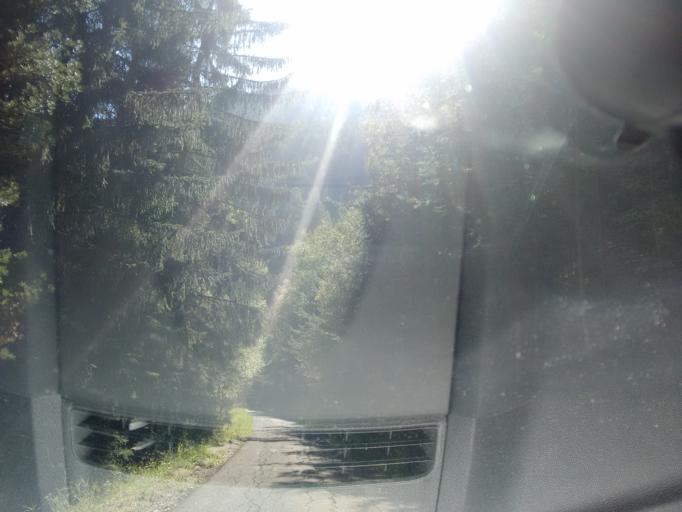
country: IT
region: Trentino-Alto Adige
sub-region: Bolzano
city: Funes - Villnoess
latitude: 46.6314
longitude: 11.6643
